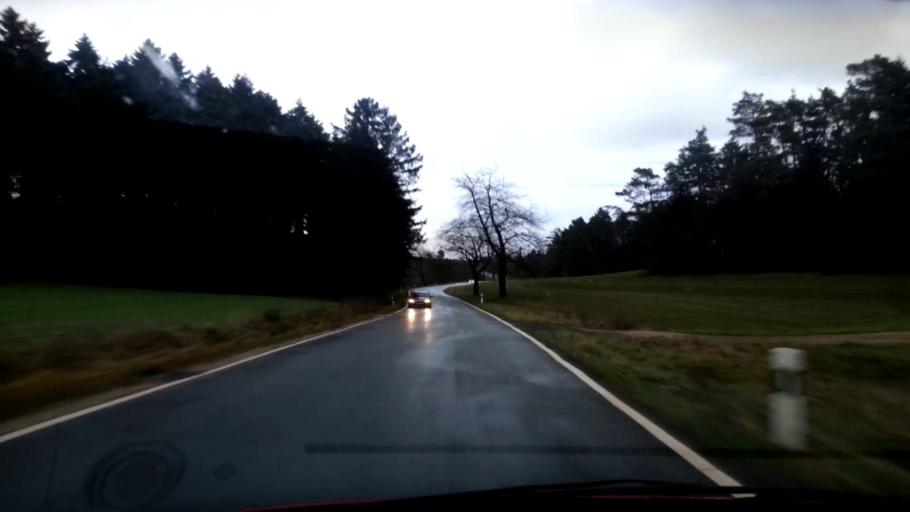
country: DE
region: Bavaria
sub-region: Upper Franconia
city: Poxdorf
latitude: 49.9238
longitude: 11.1028
